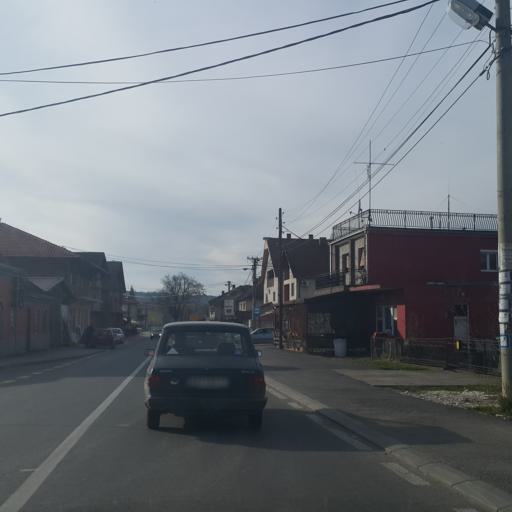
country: RS
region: Central Serbia
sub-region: Sumadijski Okrug
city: Arangelovac
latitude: 44.3369
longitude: 20.4602
